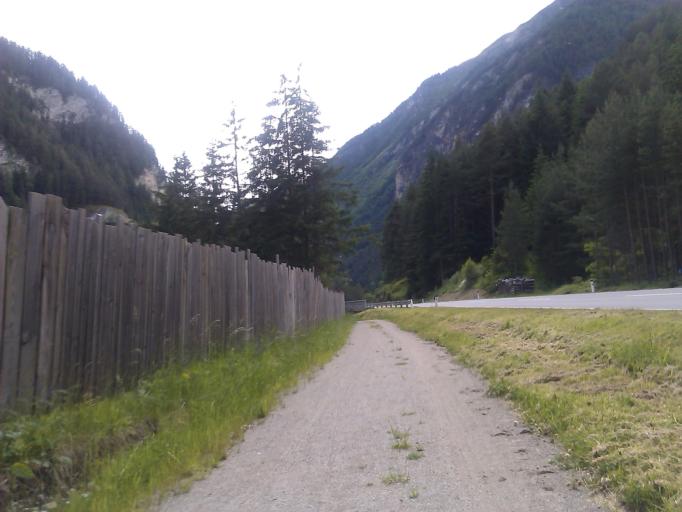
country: AT
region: Tyrol
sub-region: Politischer Bezirk Landeck
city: Pfunds
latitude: 46.9422
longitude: 10.4976
